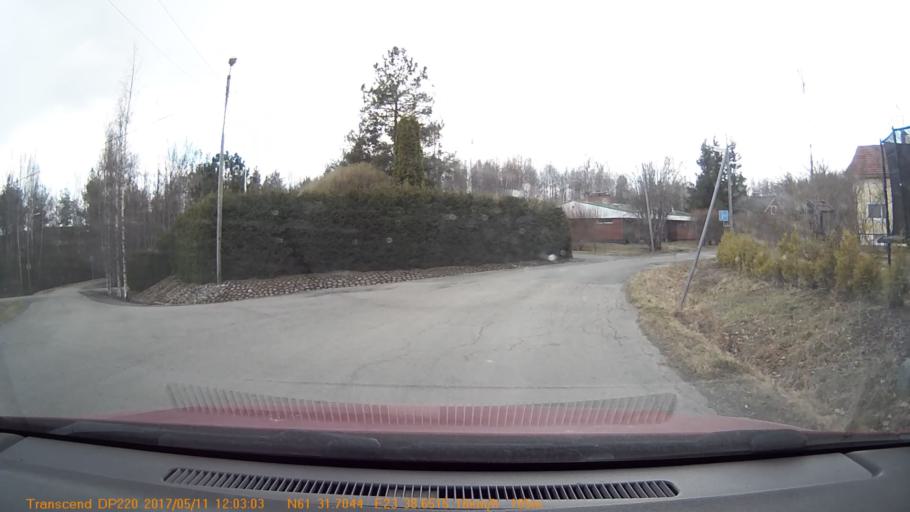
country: FI
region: Pirkanmaa
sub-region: Tampere
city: Yloejaervi
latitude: 61.5285
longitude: 23.6442
